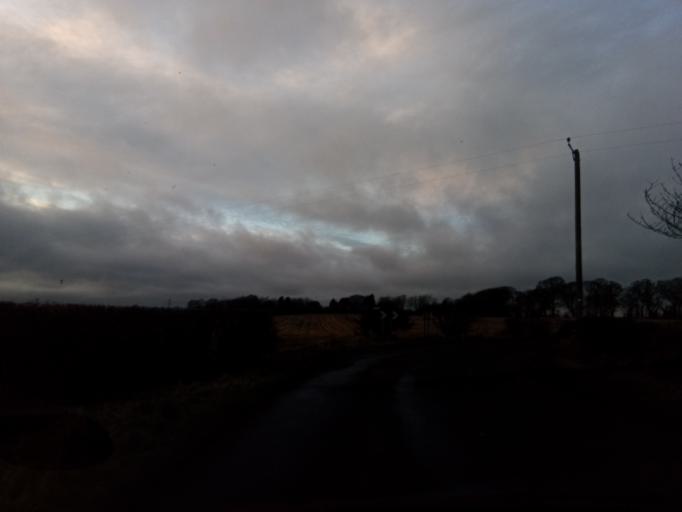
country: GB
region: England
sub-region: Northumberland
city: Meldon
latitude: 55.1333
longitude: -1.8010
